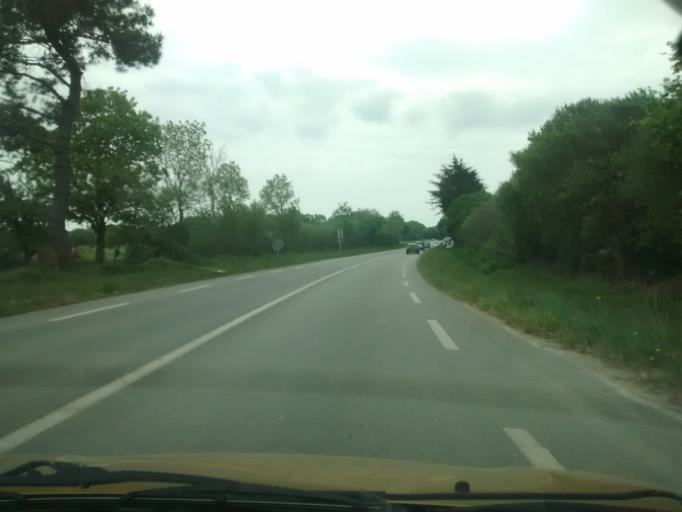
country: FR
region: Brittany
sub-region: Departement du Morbihan
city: Muzillac
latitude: 47.5534
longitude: -2.5171
